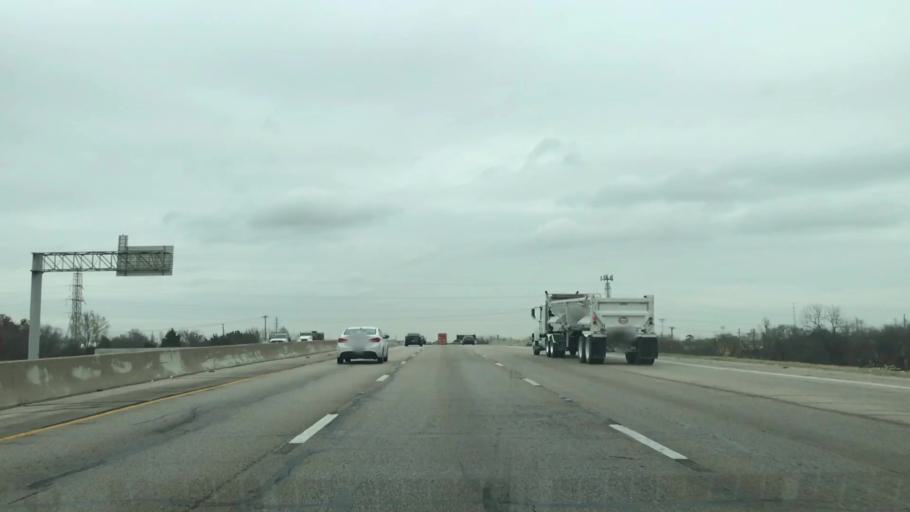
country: US
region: Texas
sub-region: Dallas County
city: Irving
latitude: 32.8123
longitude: -96.9216
